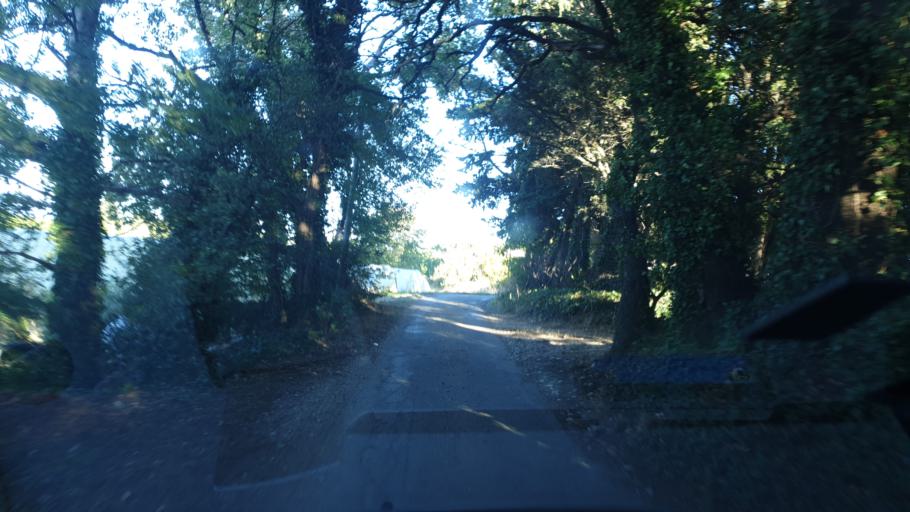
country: FR
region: Provence-Alpes-Cote d'Azur
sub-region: Departement du Vaucluse
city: Loriol-du-Comtat
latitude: 44.0584
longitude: 5.0181
